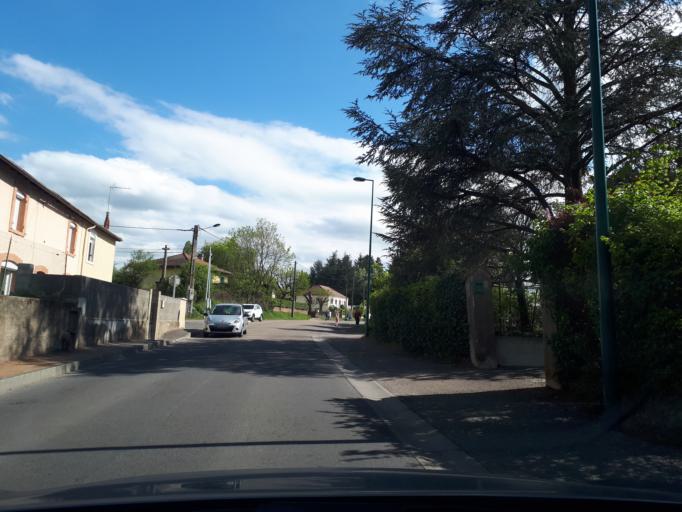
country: FR
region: Rhone-Alpes
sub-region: Departement de la Loire
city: Bellegarde-en-Forez
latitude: 45.6366
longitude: 4.3009
